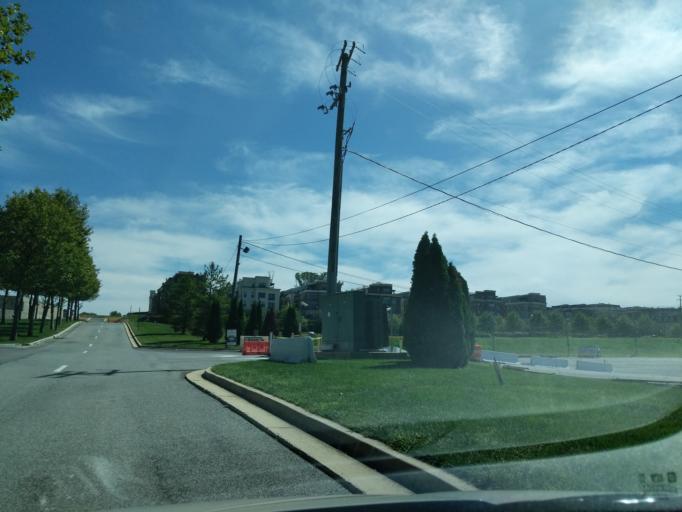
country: US
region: Maryland
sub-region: Prince George's County
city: Forest Heights
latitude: 38.7830
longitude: -77.0127
